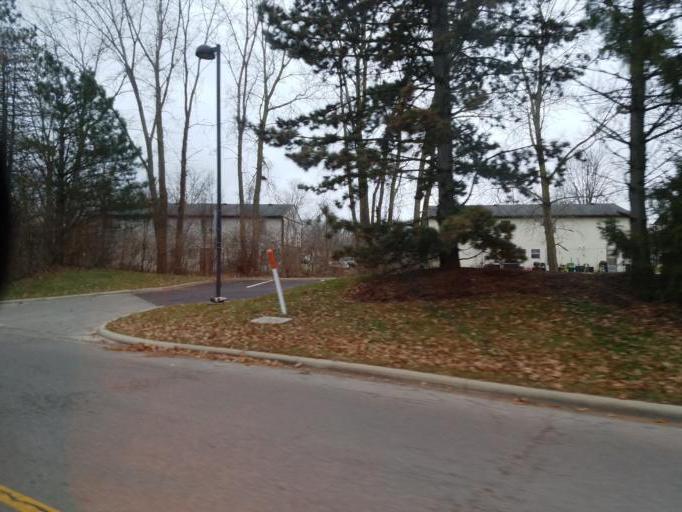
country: US
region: Ohio
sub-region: Franklin County
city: Minerva Park
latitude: 40.1018
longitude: -82.9435
